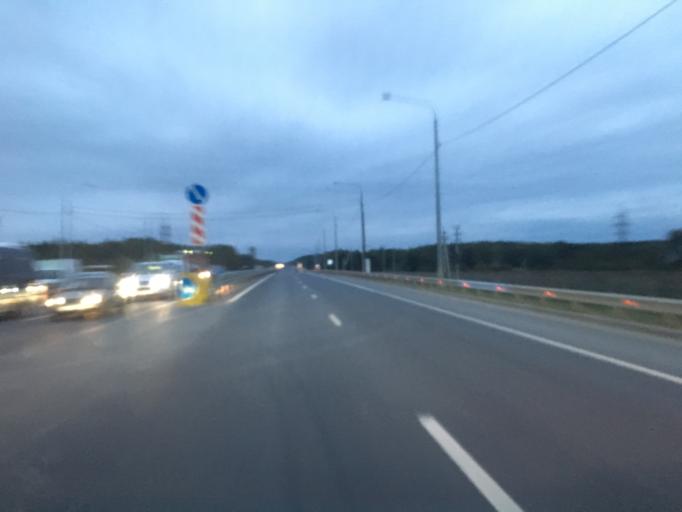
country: RU
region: Kaluga
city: Detchino
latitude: 54.9090
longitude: 36.3804
